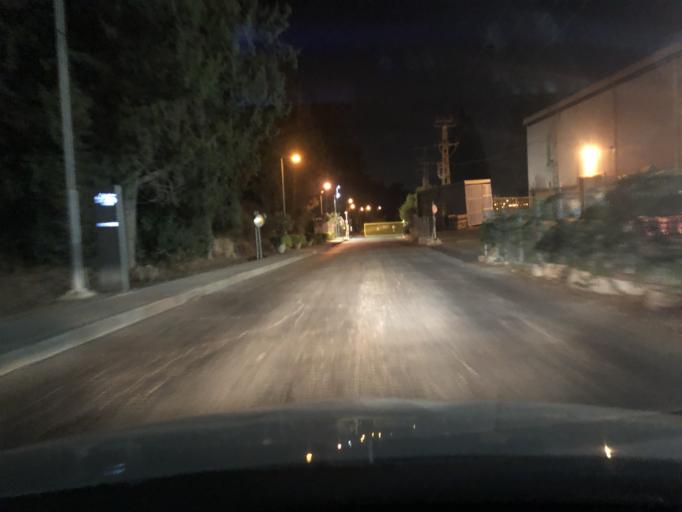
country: IL
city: Nirit
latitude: 32.1378
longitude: 34.9688
